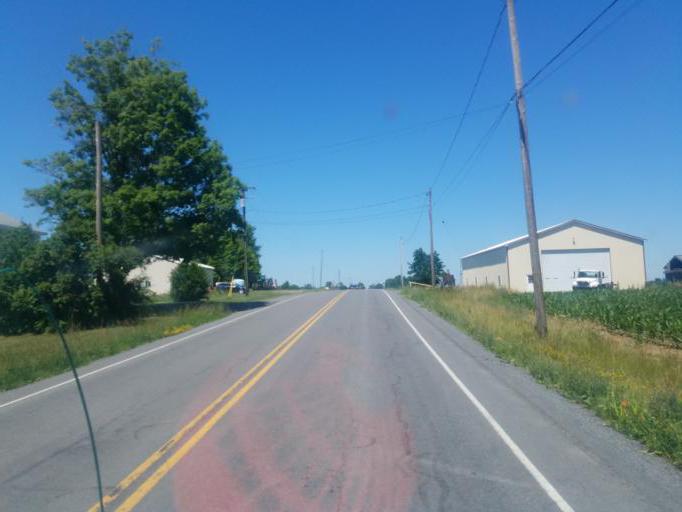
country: US
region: New York
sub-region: Yates County
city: Penn Yan
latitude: 42.7625
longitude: -77.0154
